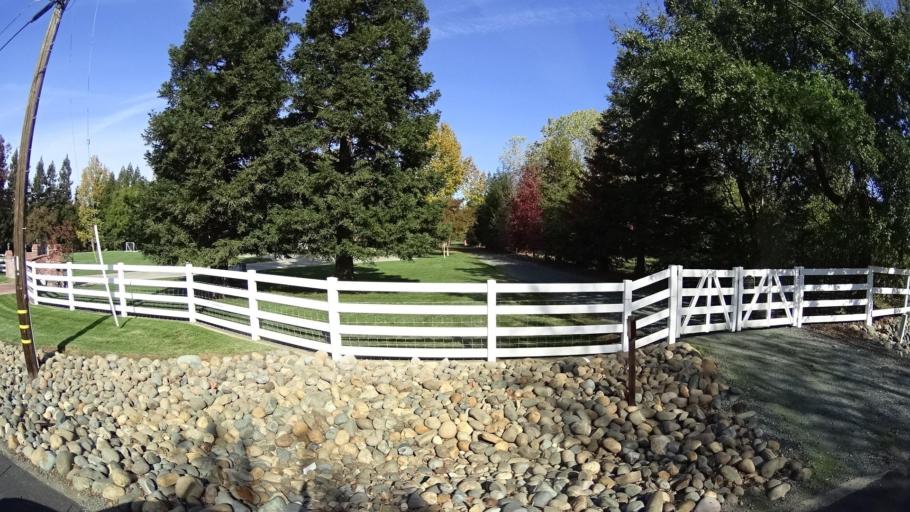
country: US
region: California
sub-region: Sacramento County
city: Wilton
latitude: 38.4299
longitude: -121.2887
